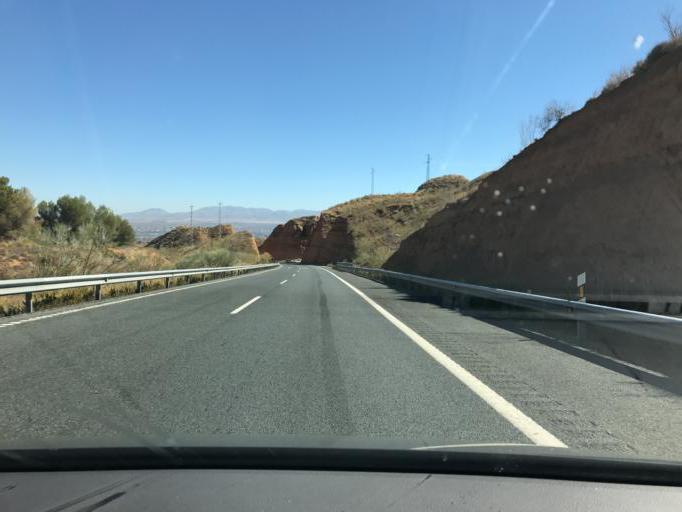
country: ES
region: Andalusia
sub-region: Provincia de Granada
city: Darro
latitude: 37.3238
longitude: -3.2521
